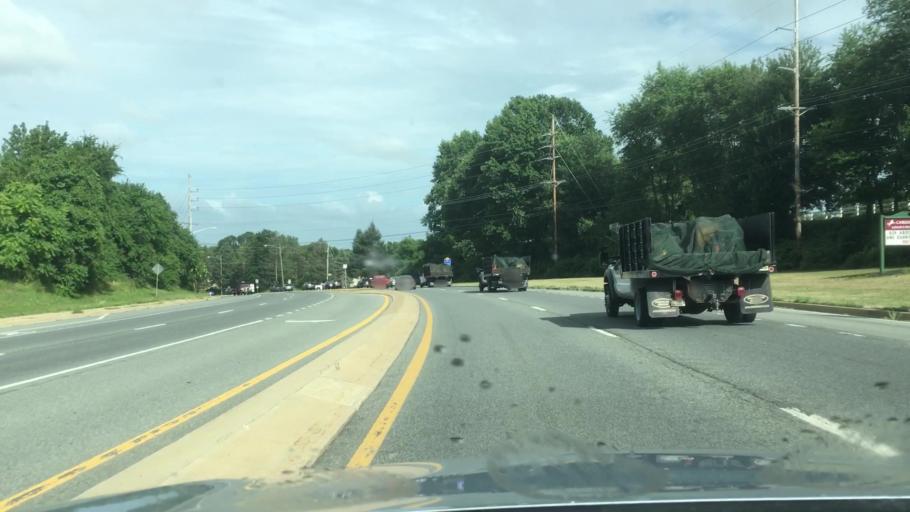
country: US
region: Delaware
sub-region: New Castle County
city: Pike Creek Valley
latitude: 39.7335
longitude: -75.6805
